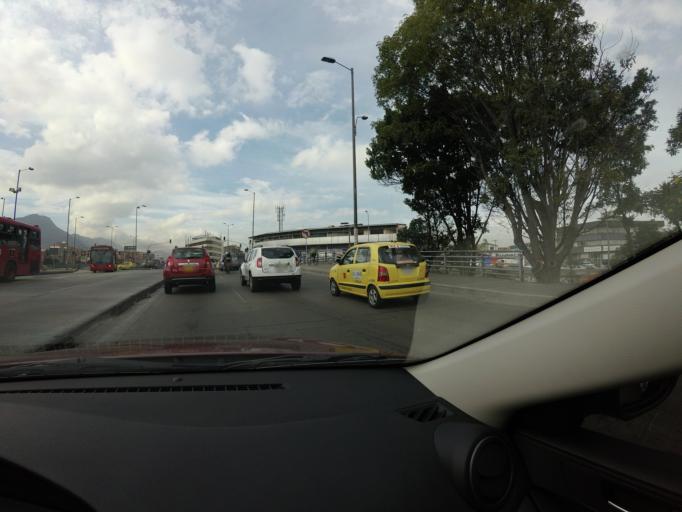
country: CO
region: Bogota D.C.
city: Barrio San Luis
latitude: 4.6654
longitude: -74.0609
